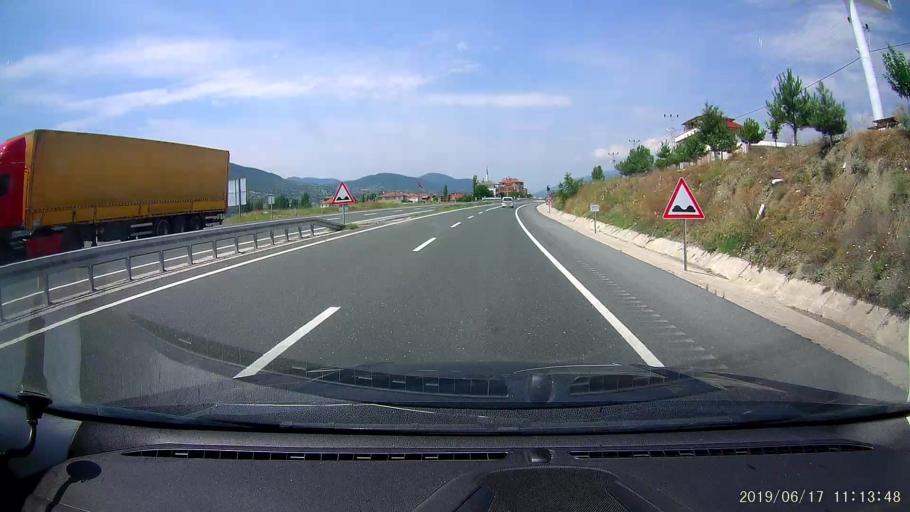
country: TR
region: Kastamonu
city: Tosya
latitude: 40.9574
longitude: 33.9642
